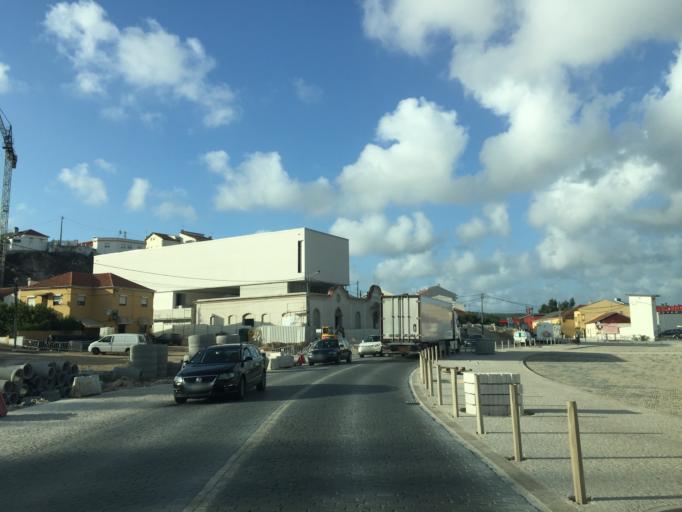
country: PT
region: Lisbon
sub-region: Torres Vedras
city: Torres Vedras
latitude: 39.1000
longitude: -9.2600
